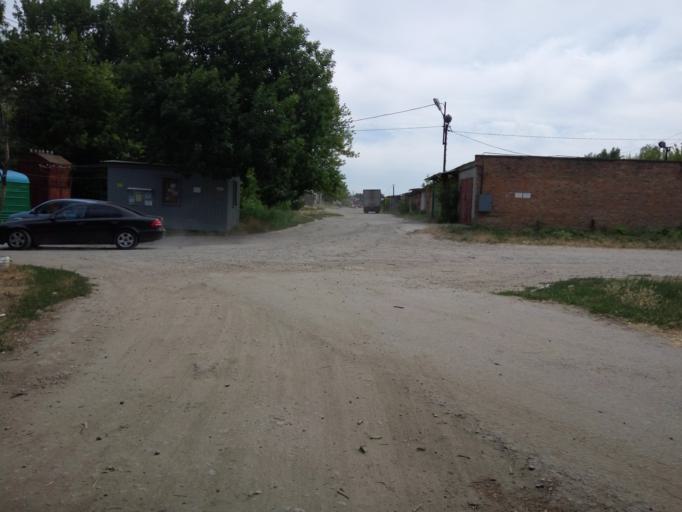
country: RU
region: Rostov
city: Bataysk
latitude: 47.1210
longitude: 39.7321
